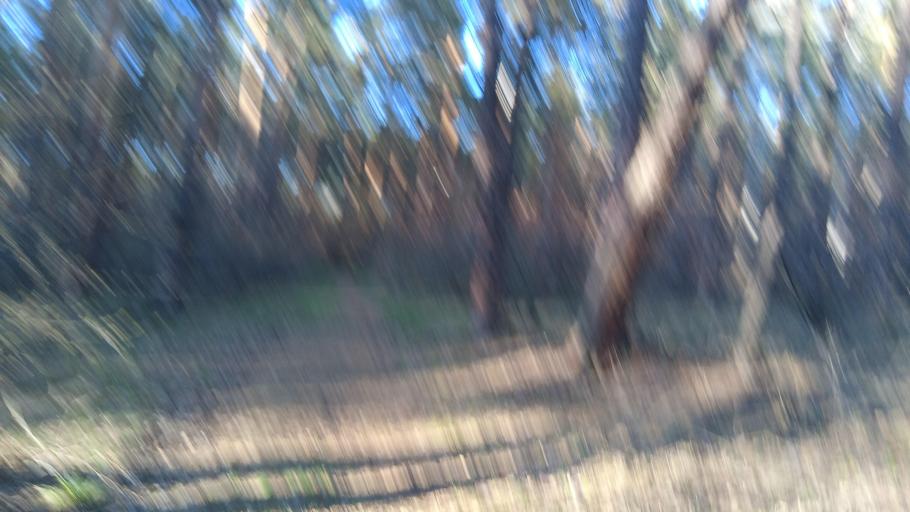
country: RU
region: Chelyabinsk
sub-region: Gorod Chelyabinsk
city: Chelyabinsk
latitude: 55.1360
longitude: 61.3295
